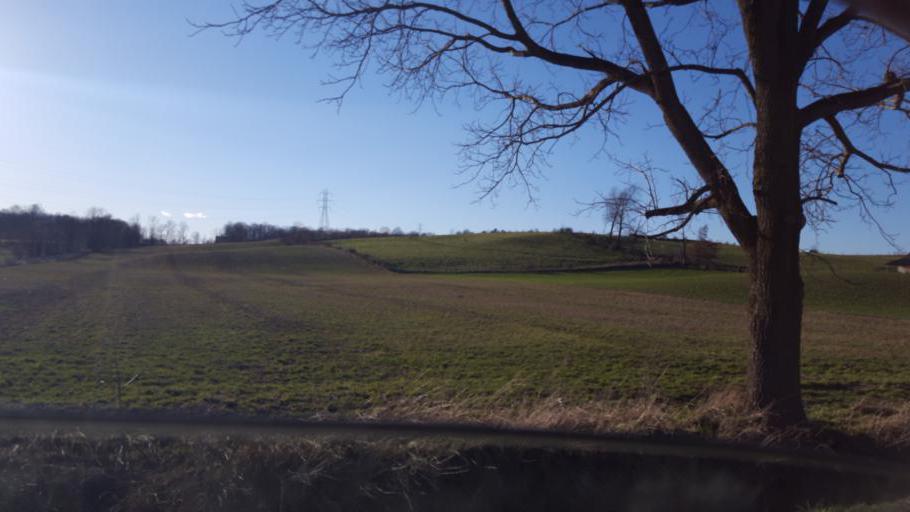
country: US
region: Ohio
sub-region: Tuscarawas County
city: Sugarcreek
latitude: 40.6078
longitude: -81.7611
